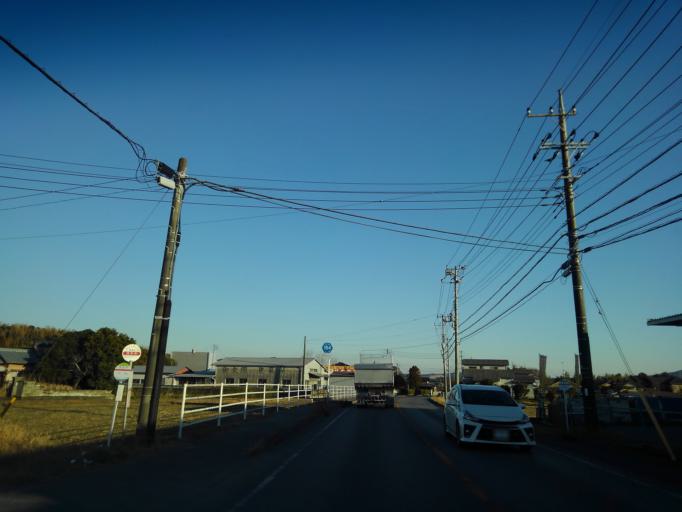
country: JP
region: Chiba
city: Kimitsu
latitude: 35.3182
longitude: 139.9285
